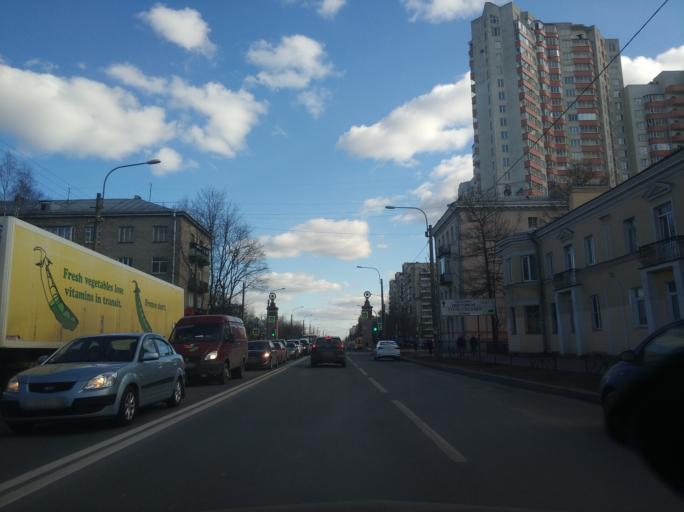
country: RU
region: St.-Petersburg
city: Krasnogvargeisky
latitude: 59.9605
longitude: 30.4900
